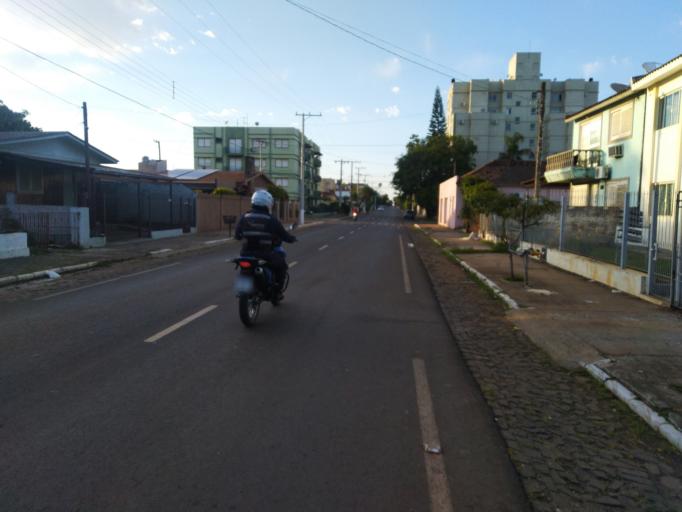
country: BR
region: Rio Grande do Sul
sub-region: Sao Borja
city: Sao Borja
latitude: -28.6538
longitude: -56.0104
